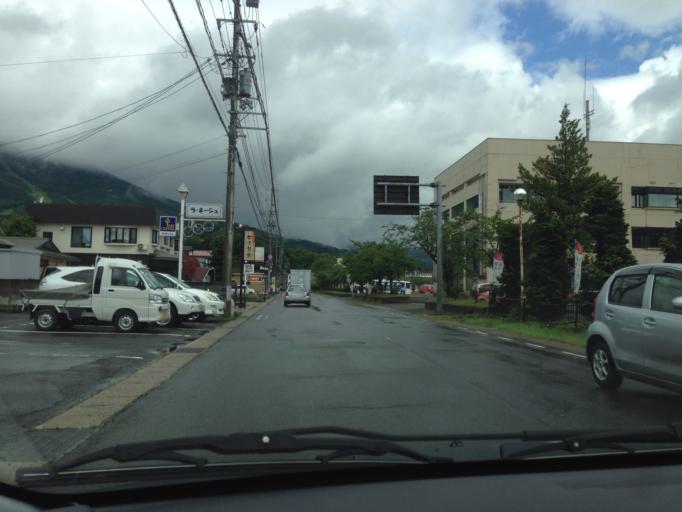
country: JP
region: Fukushima
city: Inawashiro
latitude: 37.5572
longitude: 140.1042
